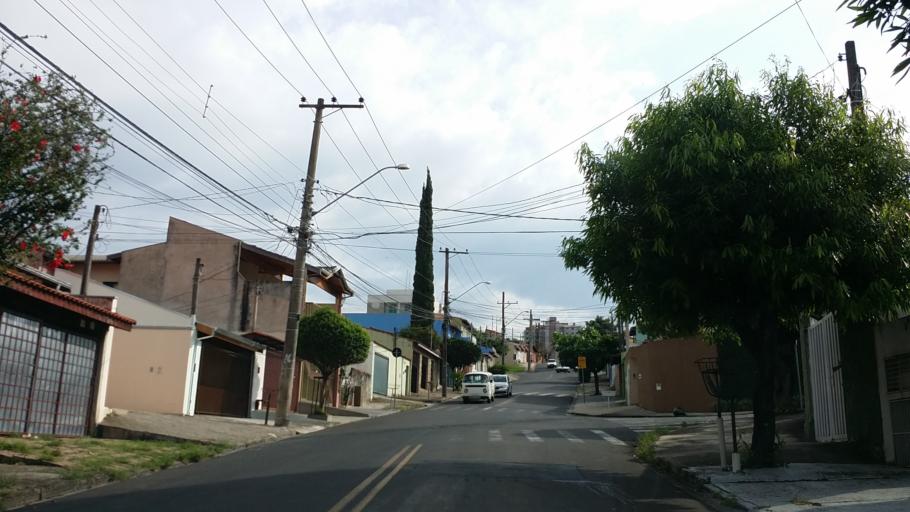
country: BR
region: Sao Paulo
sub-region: Indaiatuba
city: Indaiatuba
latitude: -23.0956
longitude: -47.2028
